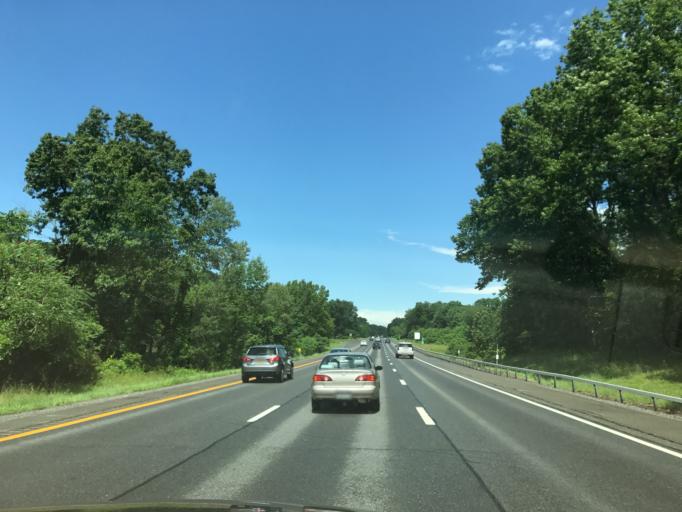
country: US
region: New York
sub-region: Saratoga County
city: Country Knolls
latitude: 42.9090
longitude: -73.7909
